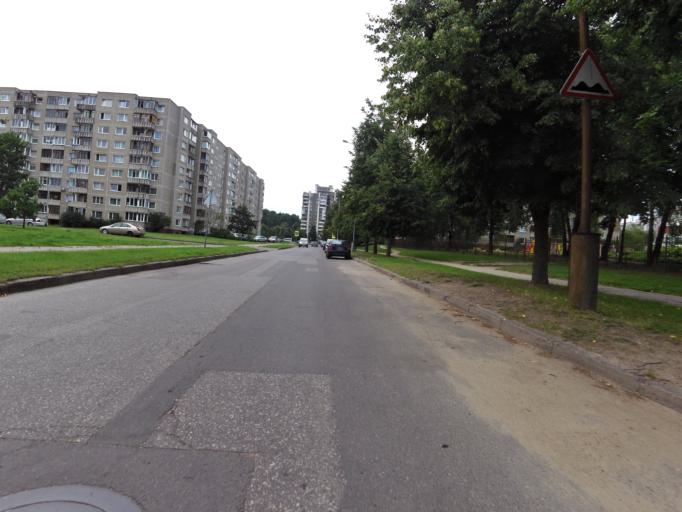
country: LT
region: Vilnius County
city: Seskine
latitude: 54.7170
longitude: 25.2411
